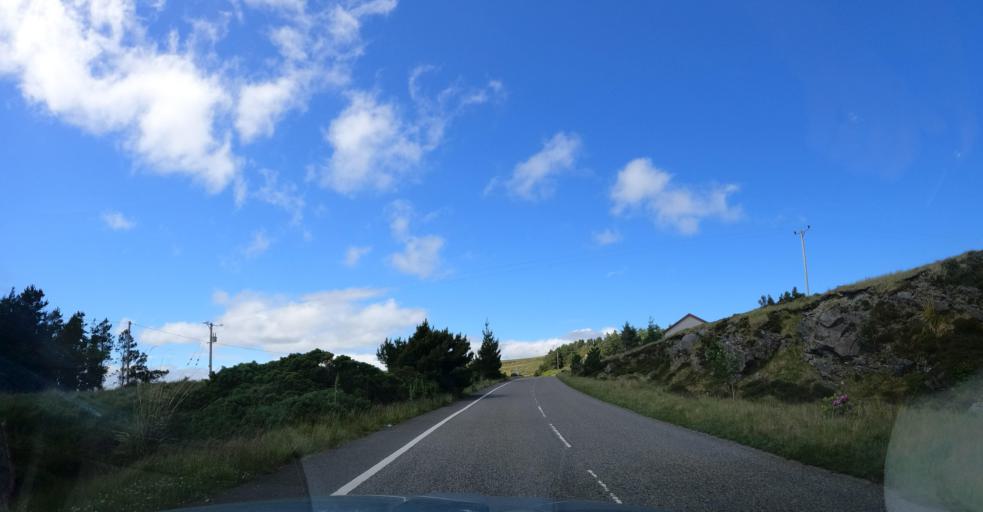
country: GB
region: Scotland
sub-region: Eilean Siar
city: Stornoway
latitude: 58.1665
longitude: -6.5613
